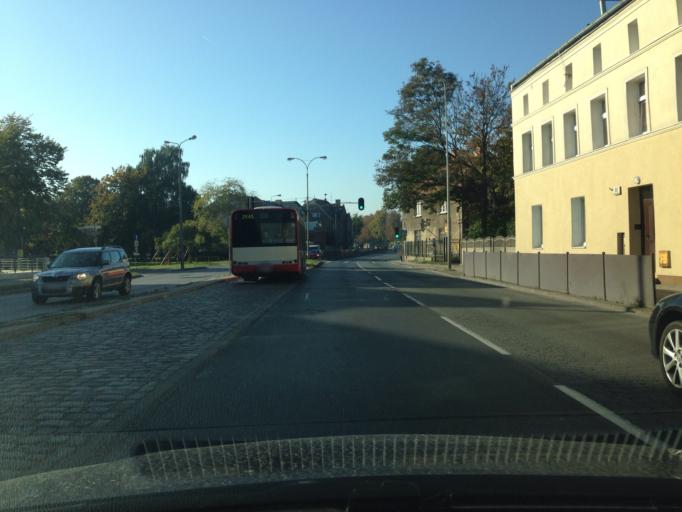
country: PL
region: Pomeranian Voivodeship
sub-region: Gdansk
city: Gdansk
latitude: 54.3243
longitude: 18.6321
